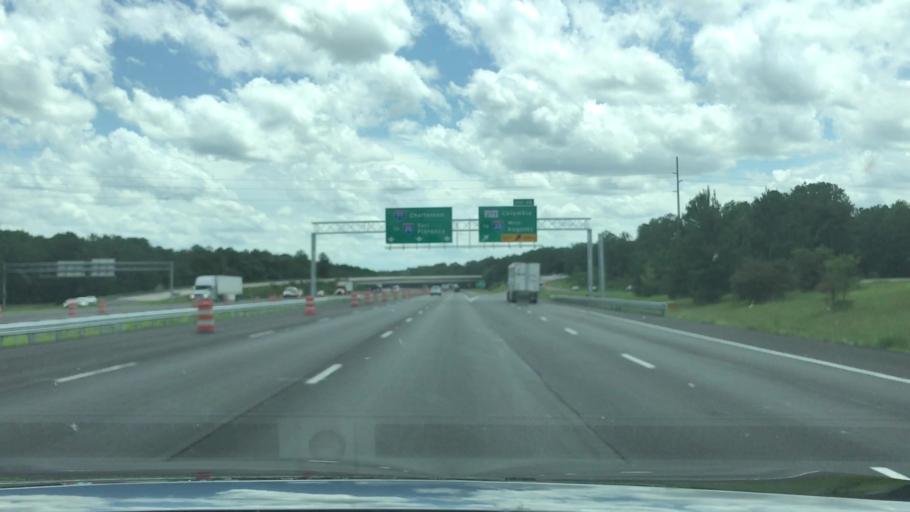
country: US
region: South Carolina
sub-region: Richland County
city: Dentsville
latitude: 34.0971
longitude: -80.9573
